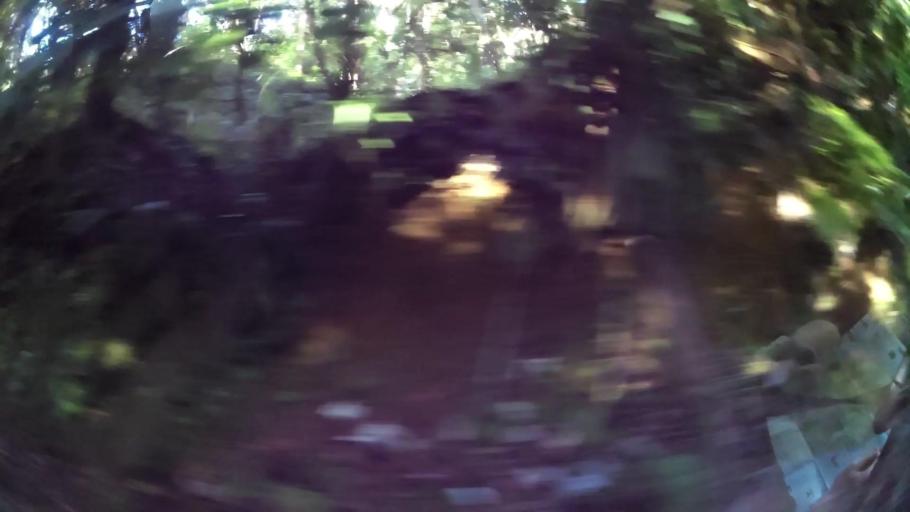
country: DM
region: Saint John
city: Portsmouth
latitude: 15.5745
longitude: -61.4324
